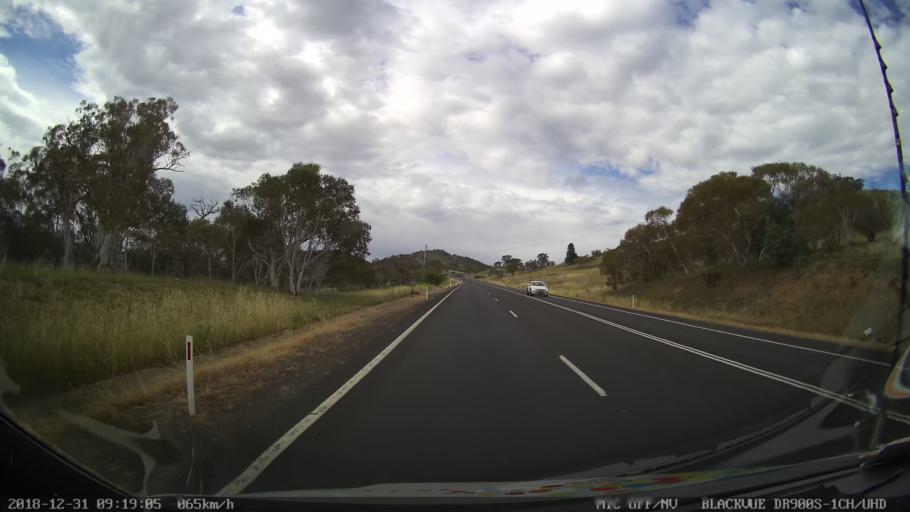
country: AU
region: New South Wales
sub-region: Snowy River
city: Jindabyne
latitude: -36.4123
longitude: 148.5881
